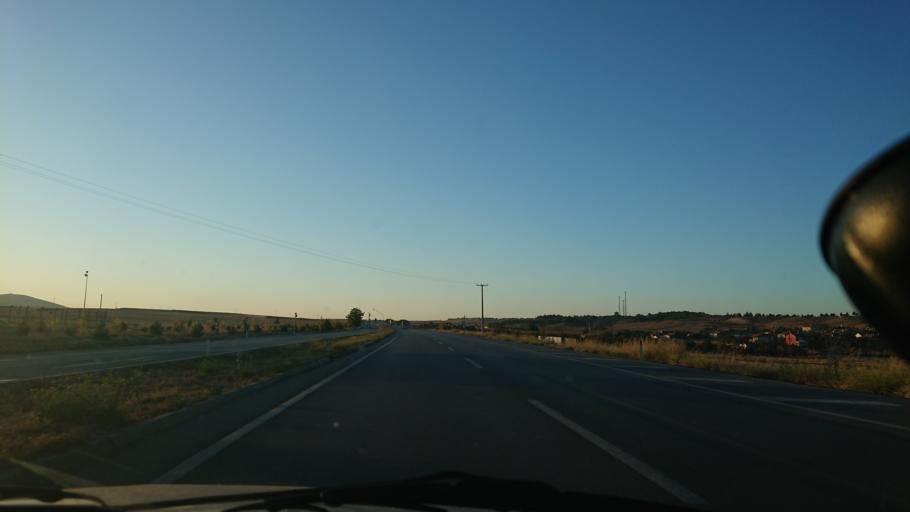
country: TR
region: Eskisehir
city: Mahmudiye
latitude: 39.4890
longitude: 30.9815
